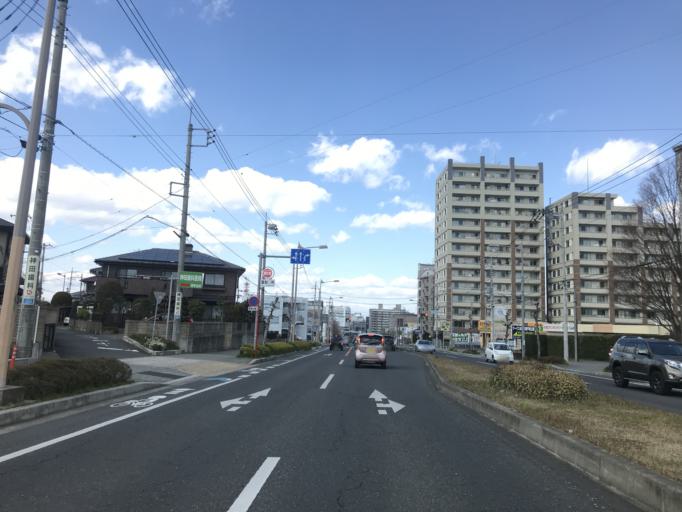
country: JP
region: Ibaraki
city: Mito-shi
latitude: 36.3596
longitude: 140.4741
